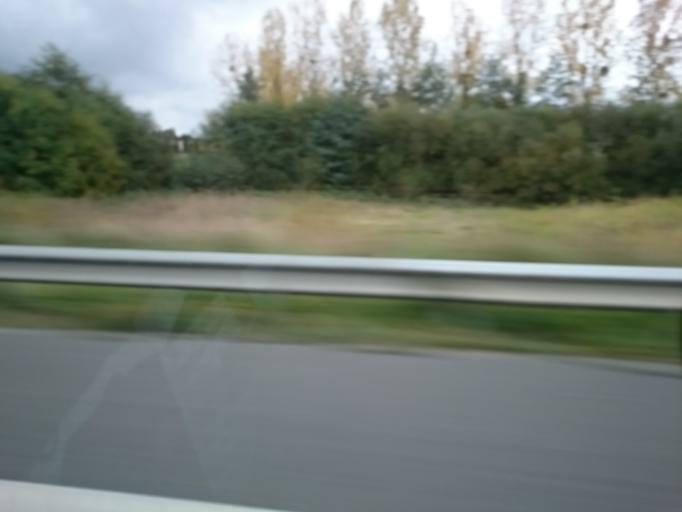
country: FR
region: Brittany
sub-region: Departement des Cotes-d'Armor
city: Sevignac
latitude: 48.3701
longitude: -2.3394
